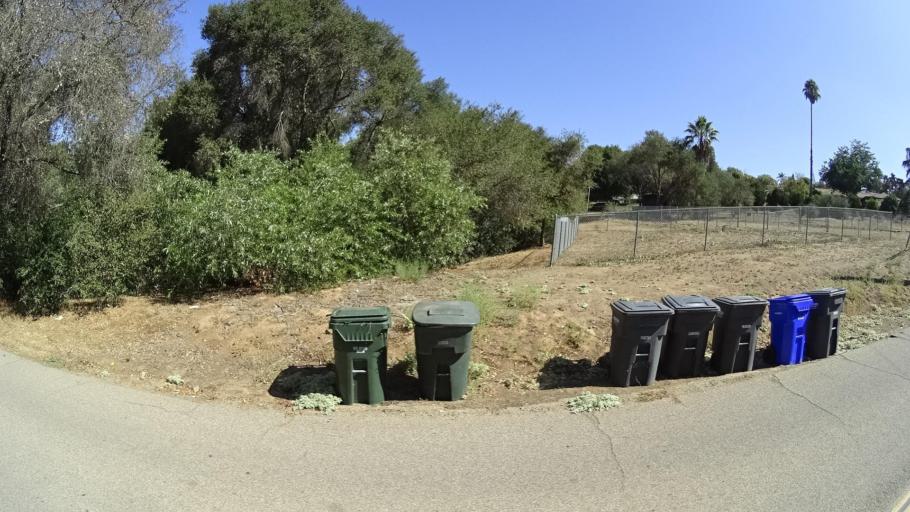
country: US
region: California
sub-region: San Diego County
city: Bonsall
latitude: 33.3271
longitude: -117.2306
